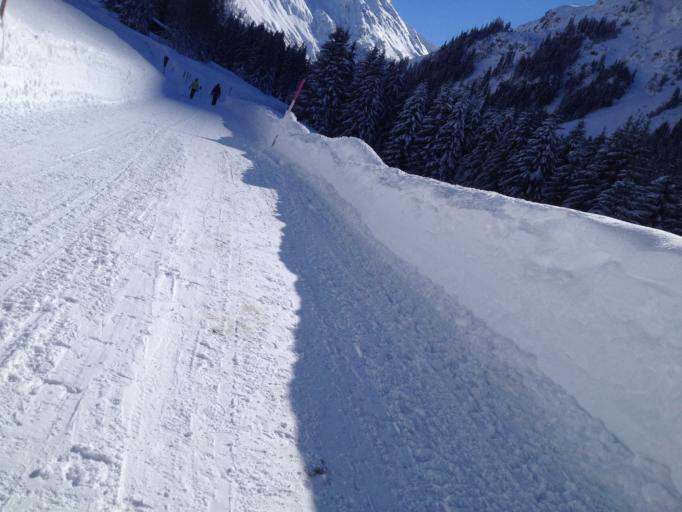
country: CH
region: Grisons
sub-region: Praettigau/Davos District
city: Klosters Serneus
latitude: 46.8612
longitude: 9.9332
